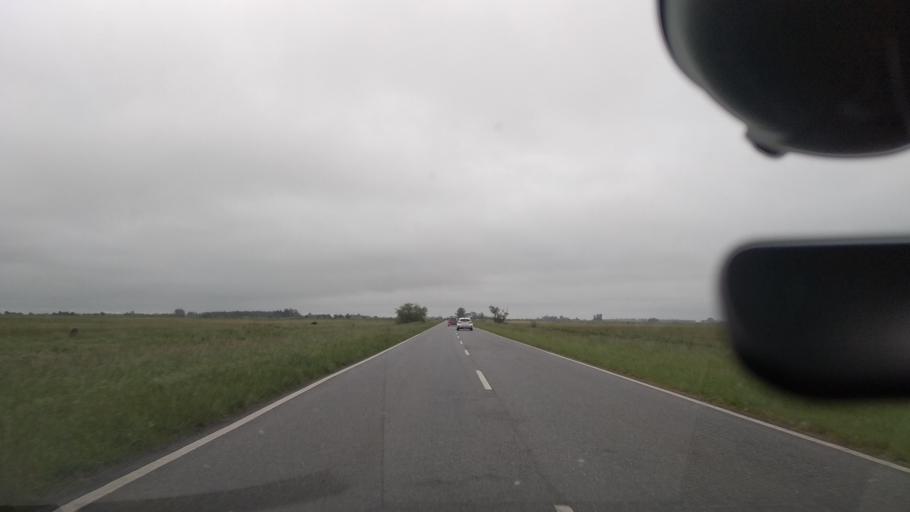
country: AR
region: Buenos Aires
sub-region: Partido de Magdalena
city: Magdalena
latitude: -35.2514
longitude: -57.6676
